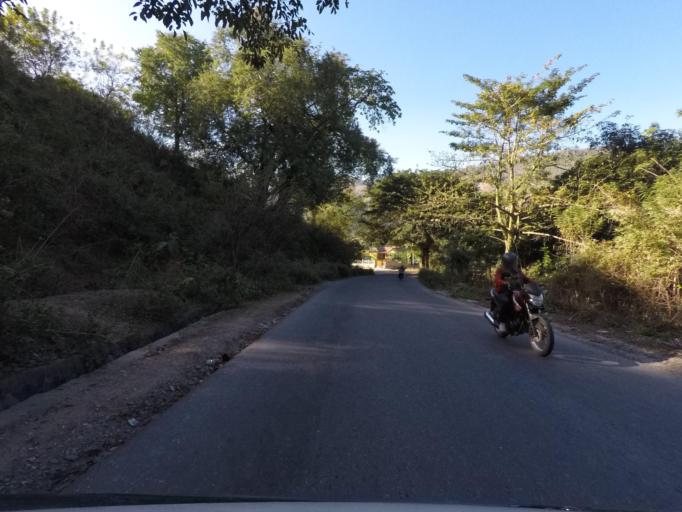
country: TL
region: Dili
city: Dili
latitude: -8.5572
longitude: 125.6448
